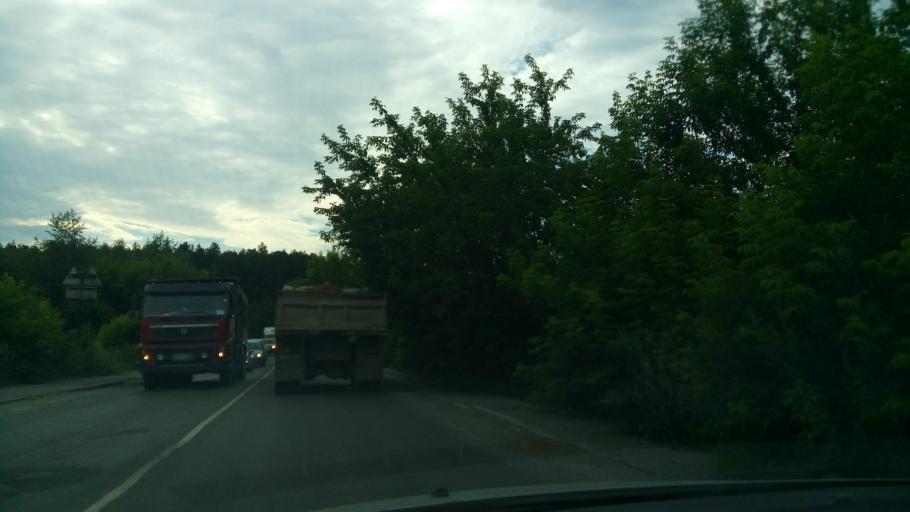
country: RU
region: Sverdlovsk
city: Yekaterinburg
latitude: 56.8847
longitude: 60.6836
